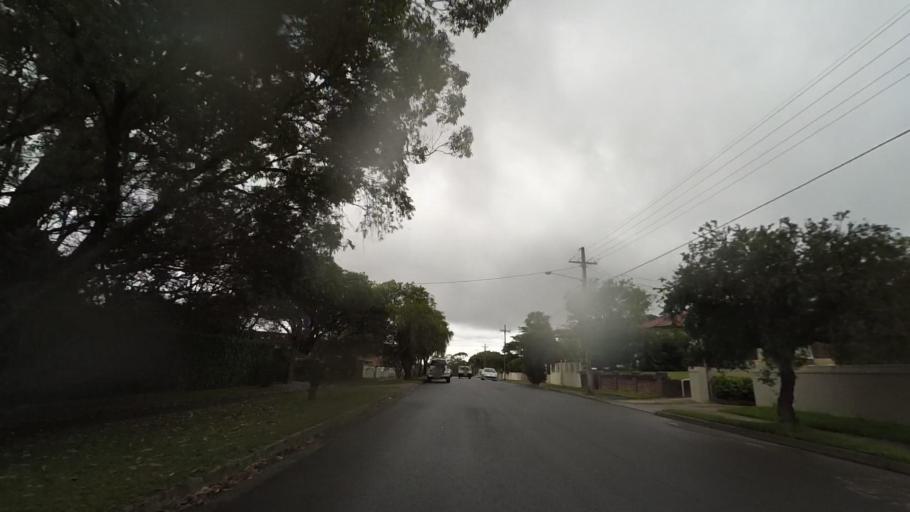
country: AU
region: New South Wales
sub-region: Kogarah
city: Kogarah
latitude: -33.9969
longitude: 151.1247
